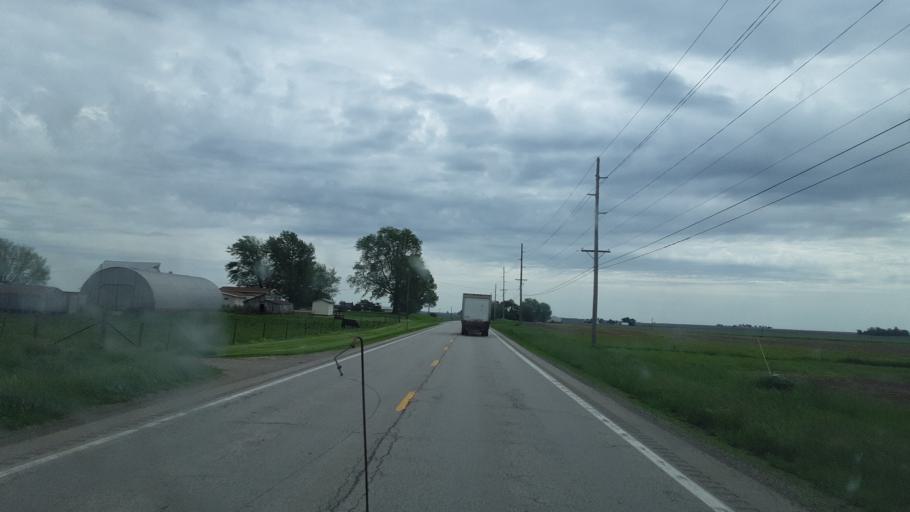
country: US
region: Illinois
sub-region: Tazewell County
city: Delavan
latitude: 40.3057
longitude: -89.5895
